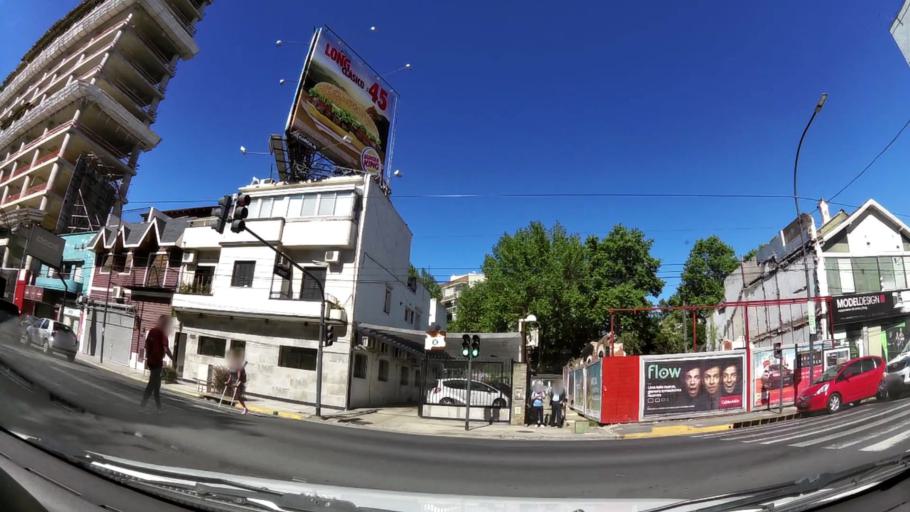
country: AR
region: Buenos Aires
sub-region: Partido de Vicente Lopez
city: Olivos
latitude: -34.5238
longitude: -58.4727
